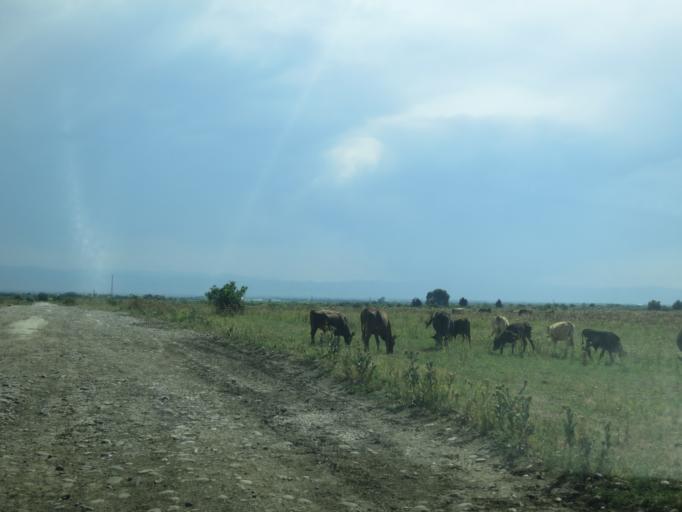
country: GE
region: Kvemo Kartli
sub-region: Gardabani
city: Gardabani
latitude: 41.4762
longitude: 45.1721
